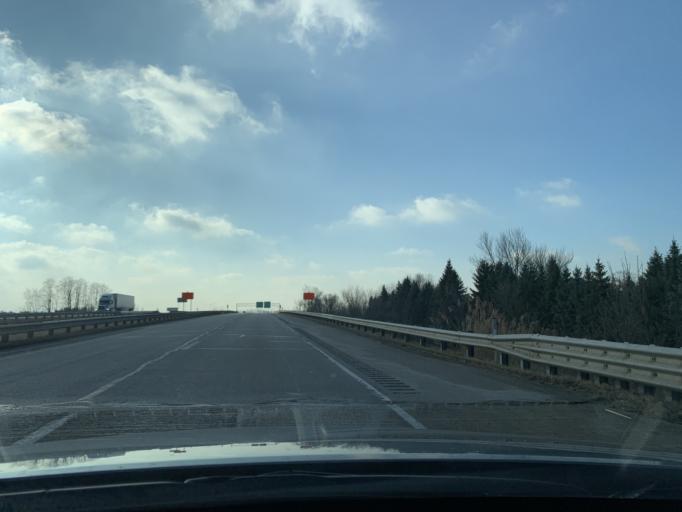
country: US
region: Indiana
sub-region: Porter County
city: Valparaiso
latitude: 41.4781
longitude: -87.0206
